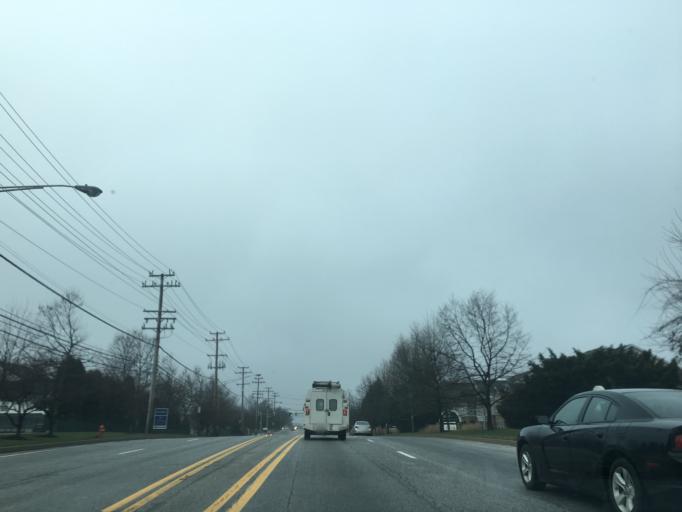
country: US
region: Maryland
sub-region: Baltimore County
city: Garrison
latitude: 39.3937
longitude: -76.7447
